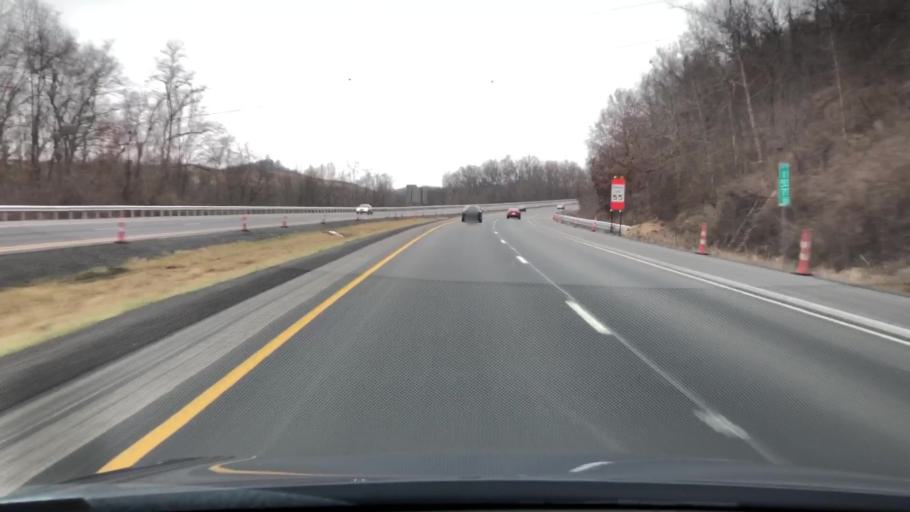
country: US
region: West Virginia
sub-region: Monongalia County
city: Star City
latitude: 39.6758
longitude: -80.0346
